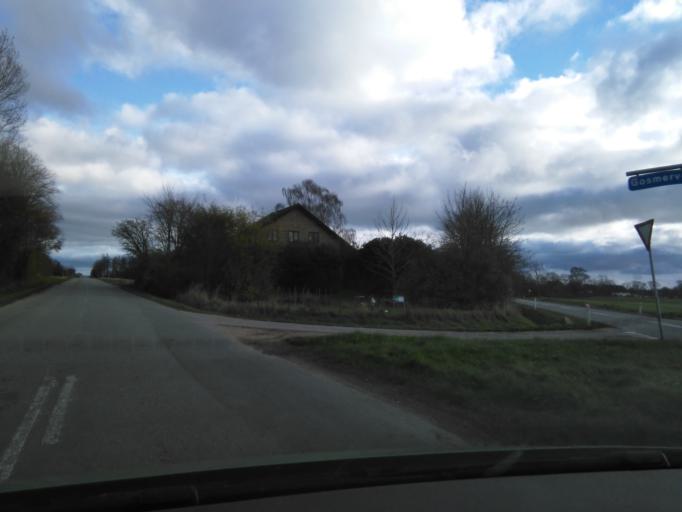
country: DK
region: Central Jutland
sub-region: Odder Kommune
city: Odder
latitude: 55.9255
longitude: 10.1560
